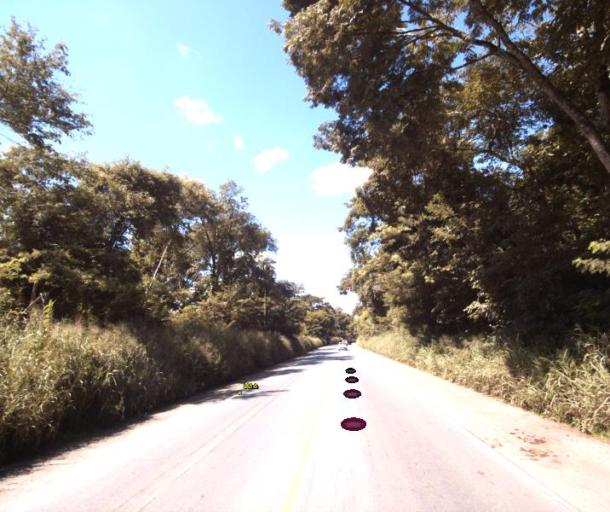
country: BR
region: Goias
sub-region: Jaragua
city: Jaragua
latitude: -15.7022
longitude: -49.3328
